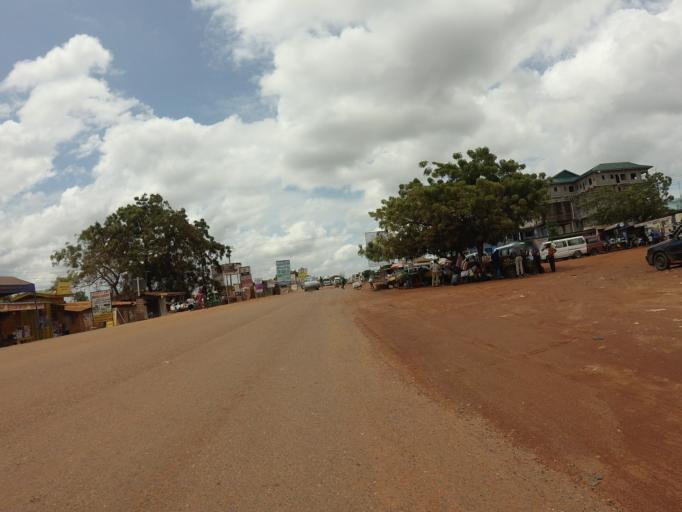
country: GH
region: Eastern
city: Aburi
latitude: 5.8162
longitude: -0.1215
